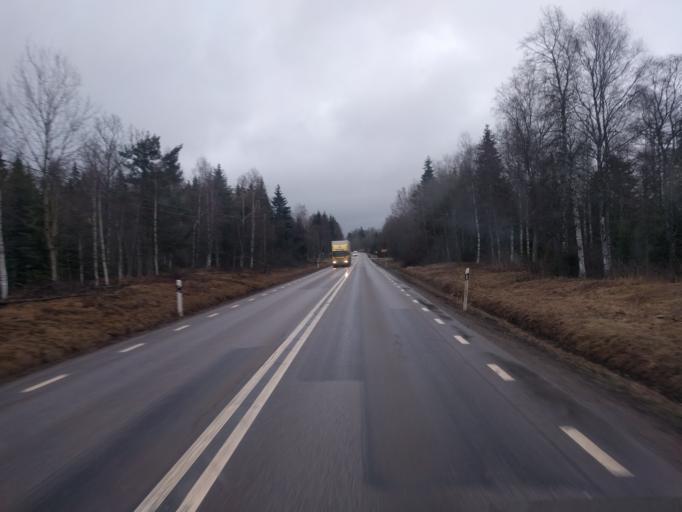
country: SE
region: Joenkoeping
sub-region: Eksjo Kommun
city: Mariannelund
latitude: 57.6344
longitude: 15.6298
